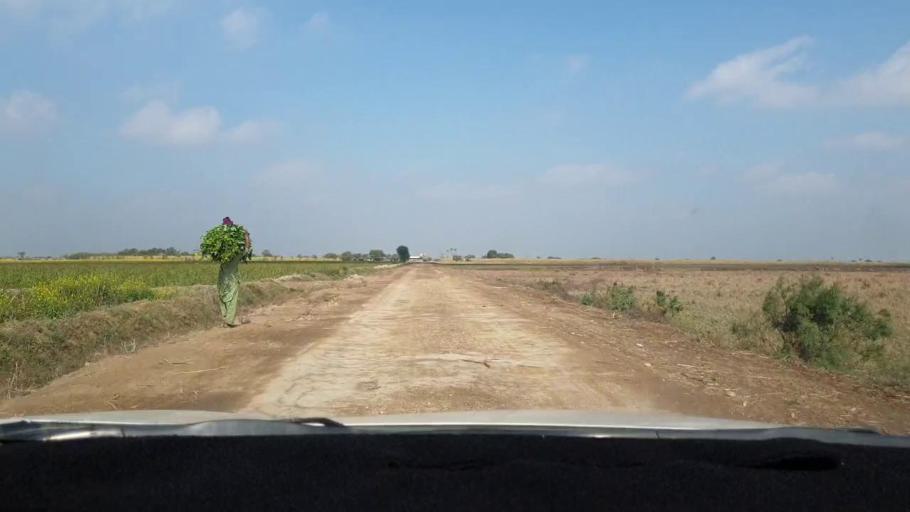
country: PK
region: Sindh
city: Berani
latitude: 25.7474
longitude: 69.0076
